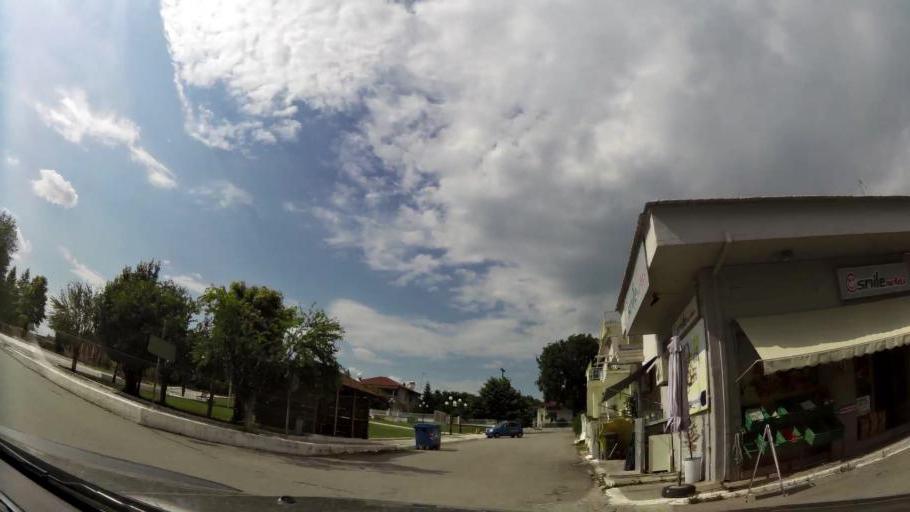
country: GR
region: Central Macedonia
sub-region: Nomos Pierias
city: Makrygialos
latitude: 40.4153
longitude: 22.6036
